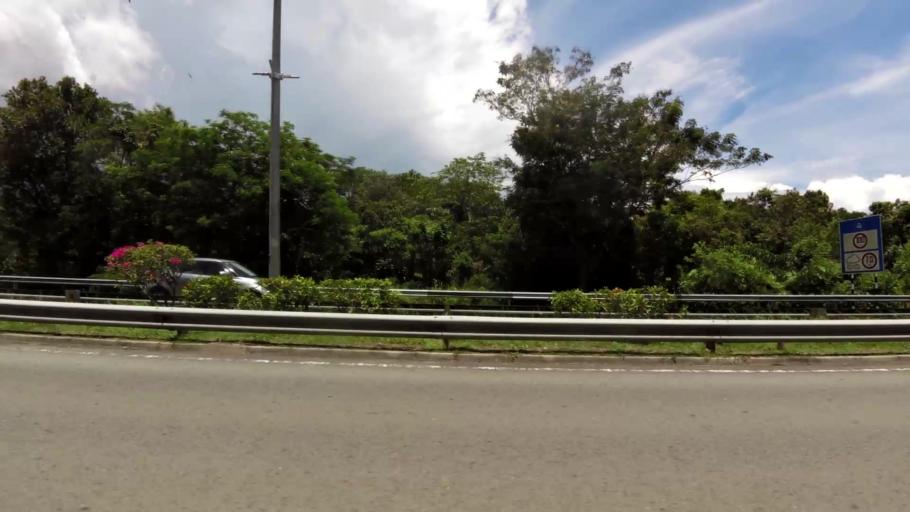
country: BN
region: Brunei and Muara
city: Bandar Seri Begawan
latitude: 4.9479
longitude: 114.9057
